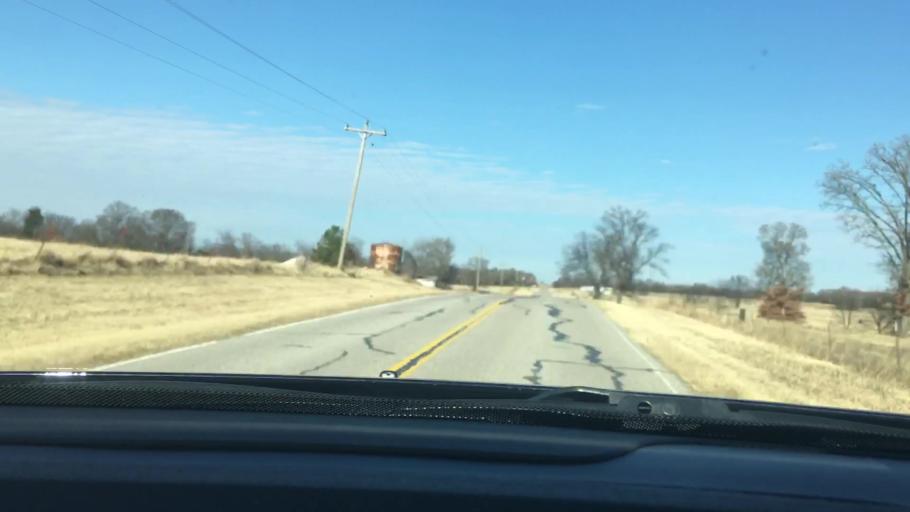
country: US
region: Oklahoma
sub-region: Garvin County
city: Wynnewood
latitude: 34.7255
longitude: -97.1255
